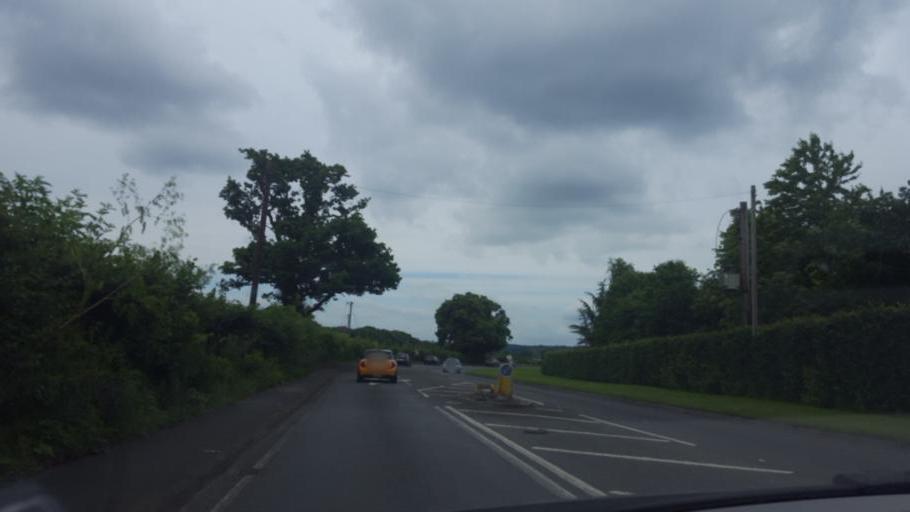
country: GB
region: England
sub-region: Royal Borough of Windsor and Maidenhead
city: Hurley
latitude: 51.5412
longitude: -0.8246
